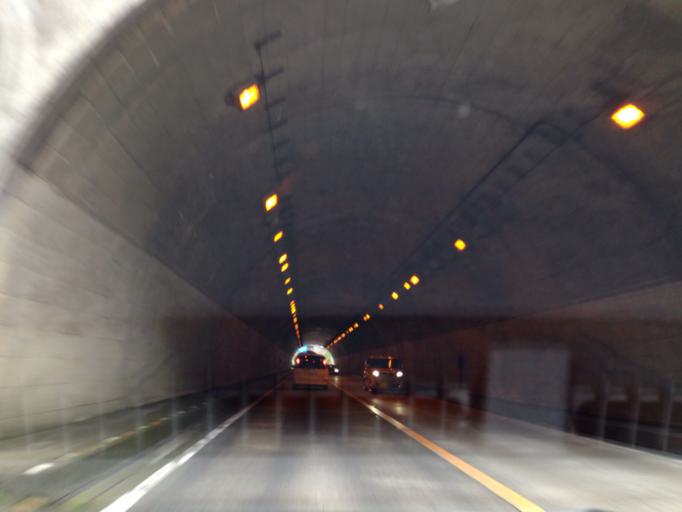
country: JP
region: Shizuoka
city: Mishima
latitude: 35.0319
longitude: 138.9229
